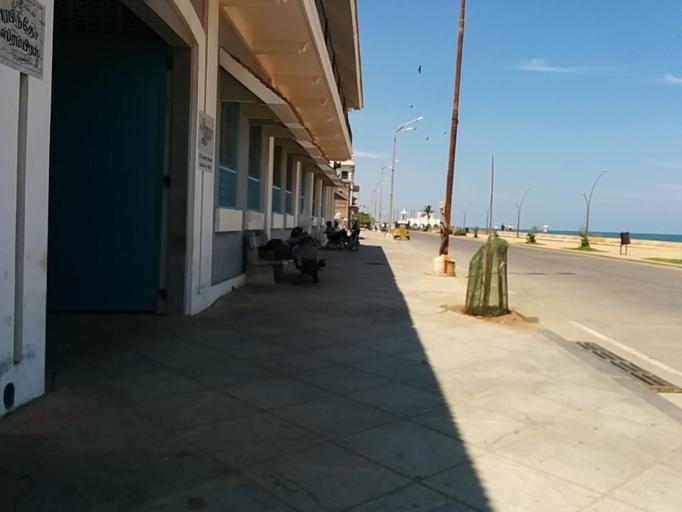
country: IN
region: Pondicherry
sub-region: Puducherry
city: Puducherry
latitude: 11.9293
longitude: 79.8351
